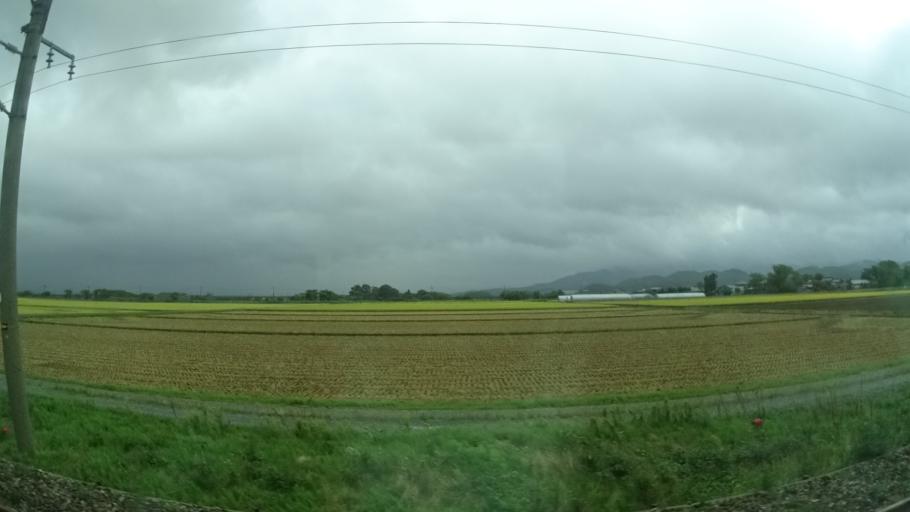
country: JP
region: Yamagata
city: Tsuruoka
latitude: 38.7319
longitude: 139.7500
